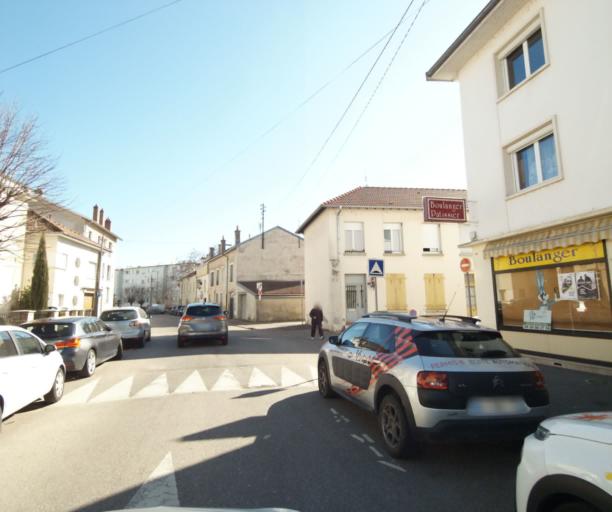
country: FR
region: Lorraine
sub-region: Departement de Meurthe-et-Moselle
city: Tomblaine
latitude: 48.6852
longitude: 6.2121
